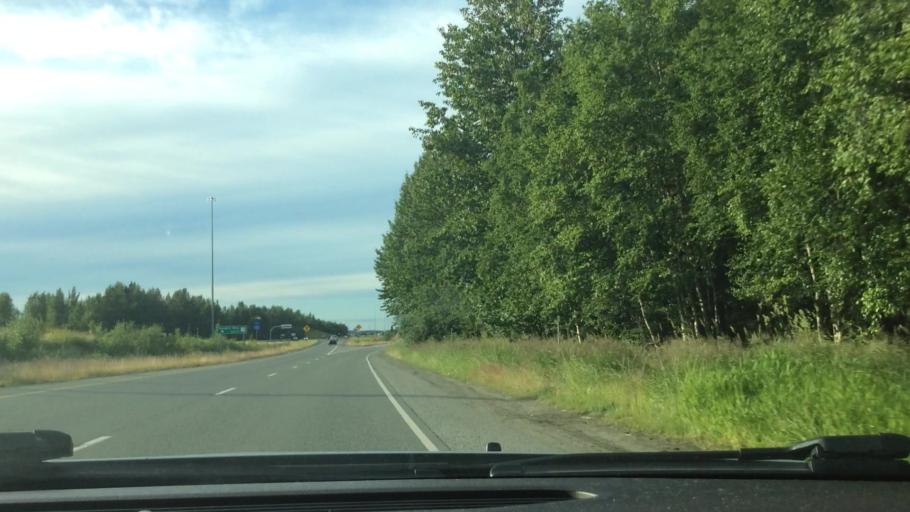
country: US
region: Alaska
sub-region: Anchorage Municipality
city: Anchorage
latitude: 61.1245
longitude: -149.8557
